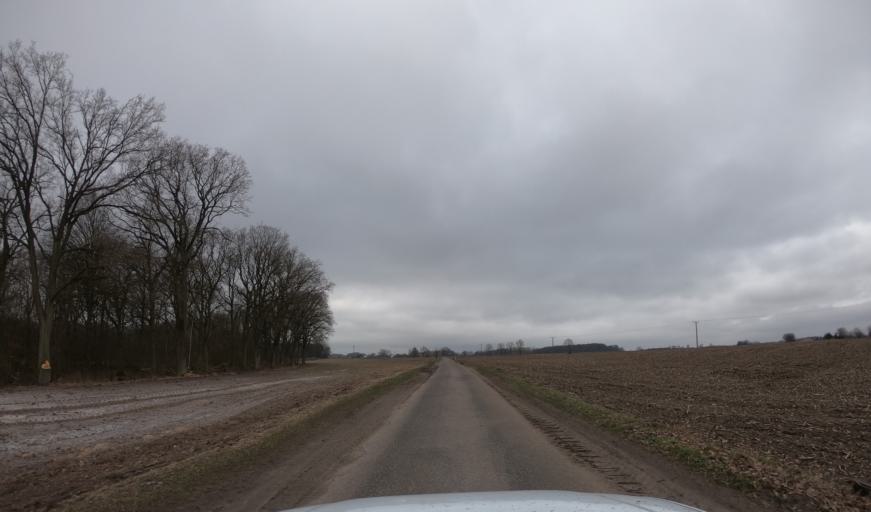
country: PL
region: West Pomeranian Voivodeship
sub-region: Powiat gryficki
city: Cerkwica
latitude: 53.9905
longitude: 15.1027
